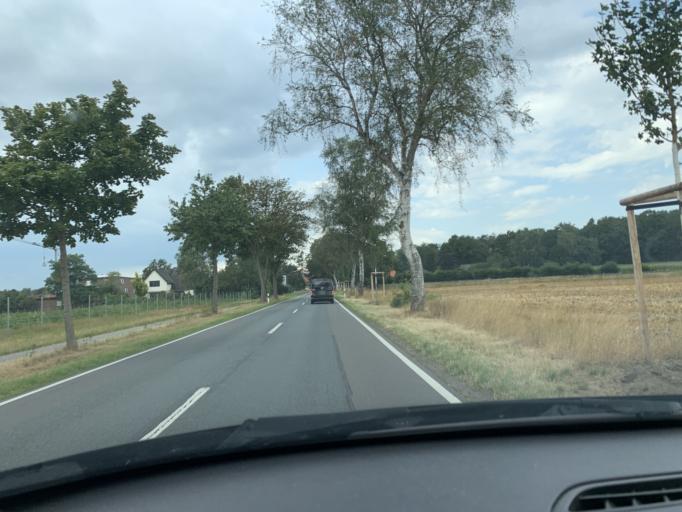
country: DE
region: Lower Saxony
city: Heidenau
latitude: 53.3108
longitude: 9.6648
